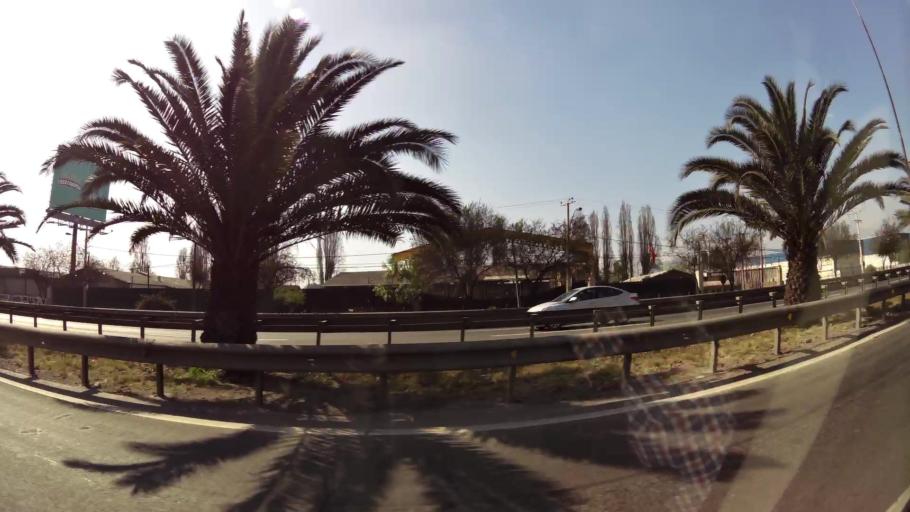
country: CL
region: Santiago Metropolitan
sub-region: Provincia de Santiago
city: Lo Prado
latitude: -33.3738
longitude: -70.7196
